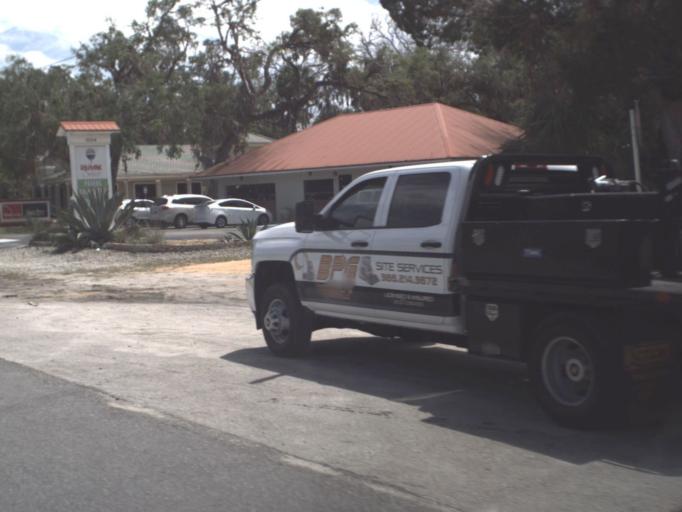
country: US
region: Florida
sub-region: Flagler County
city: Palm Coast
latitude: 29.5895
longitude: -81.1916
